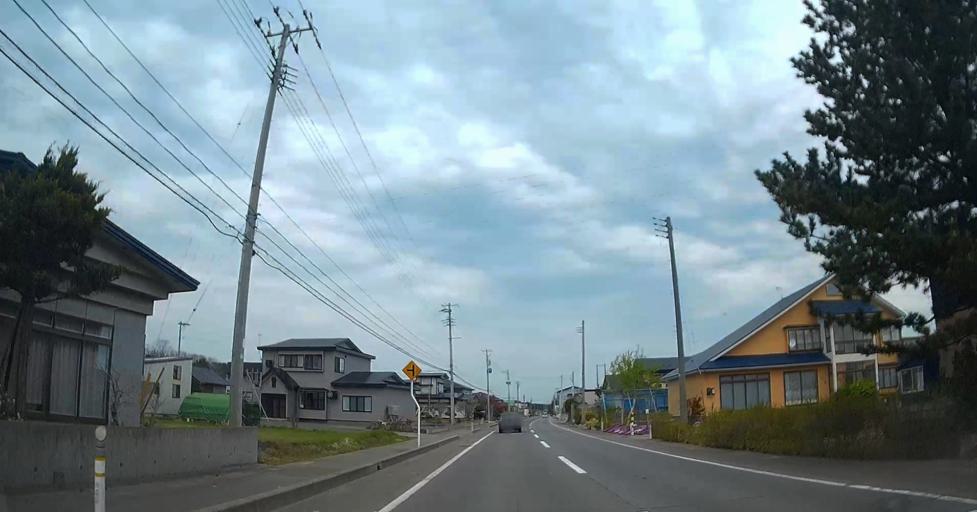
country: JP
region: Aomori
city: Shimokizukuri
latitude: 41.0012
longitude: 140.3426
